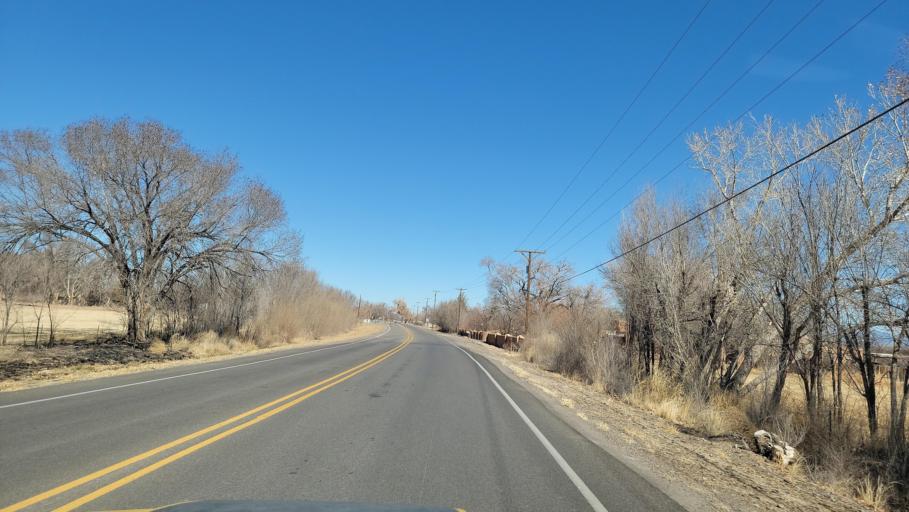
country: US
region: New Mexico
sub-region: Valencia County
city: Bosque Farms
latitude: 34.9163
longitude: -106.6930
